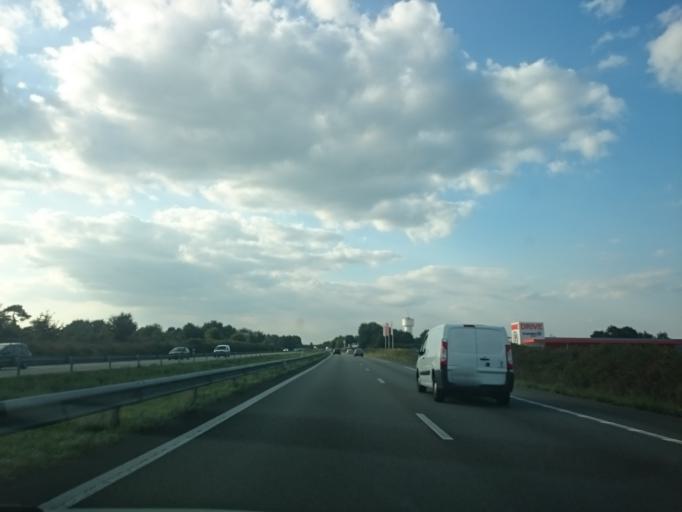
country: FR
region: Pays de la Loire
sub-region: Departement de la Loire-Atlantique
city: Sautron
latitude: 47.2756
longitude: -1.7206
